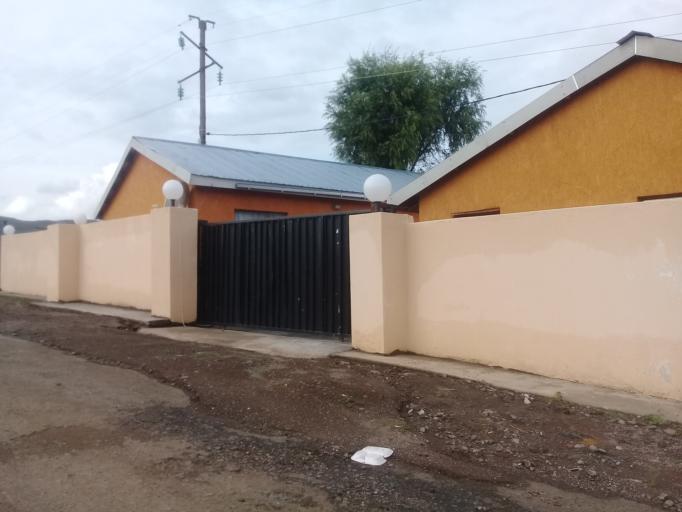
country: LS
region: Mokhotlong
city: Mokhotlong
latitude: -29.2811
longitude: 29.0657
